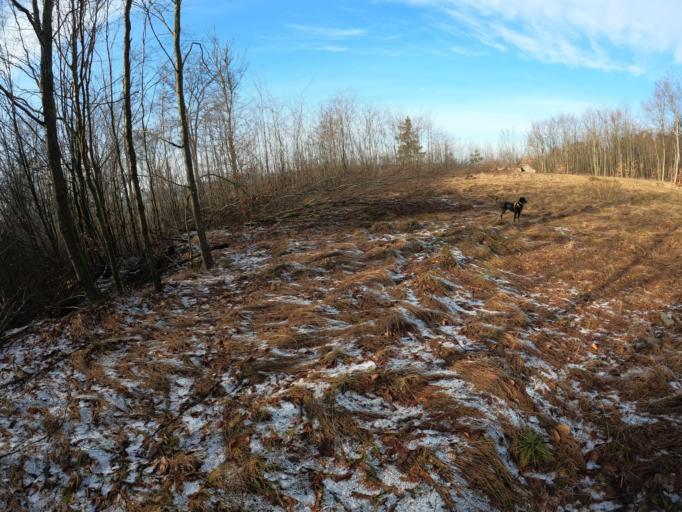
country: PL
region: West Pomeranian Voivodeship
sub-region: Powiat koszalinski
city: Polanow
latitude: 54.1223
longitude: 16.6993
